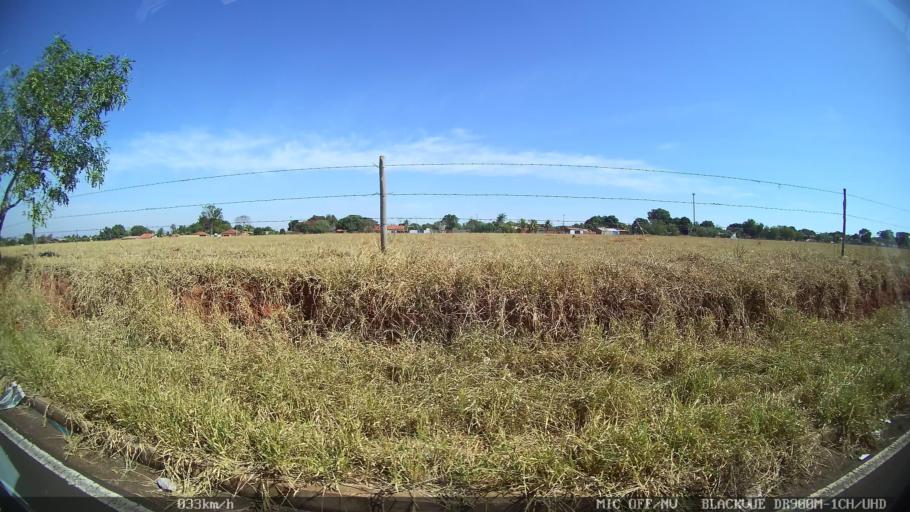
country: BR
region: Sao Paulo
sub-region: Sao Jose Do Rio Preto
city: Sao Jose do Rio Preto
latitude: -20.7557
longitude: -49.4243
